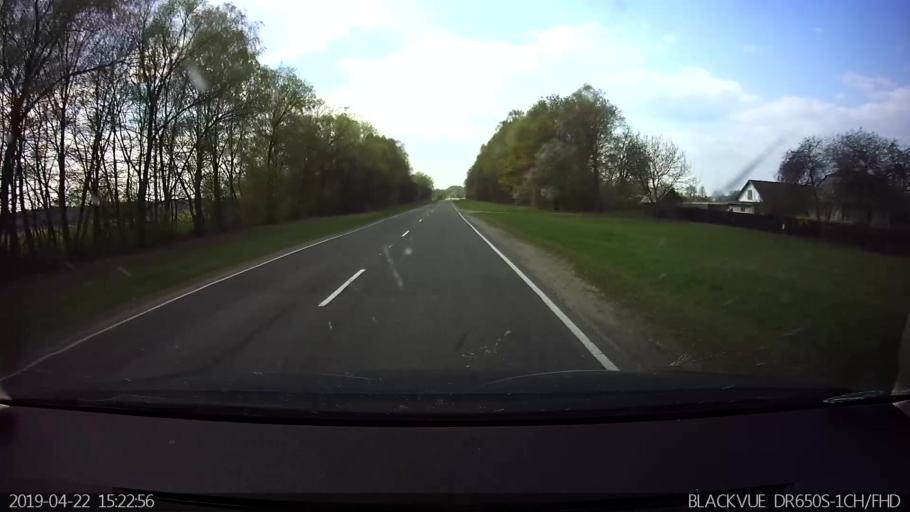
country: BY
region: Brest
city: Vysokaye
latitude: 52.3524
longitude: 23.4361
